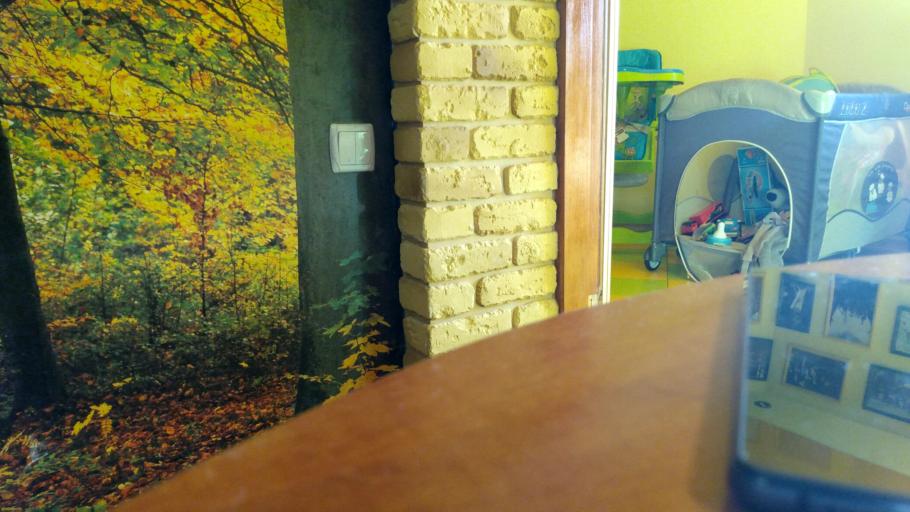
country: RU
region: Tverskaya
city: Likhoslavl'
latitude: 57.1600
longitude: 35.5908
